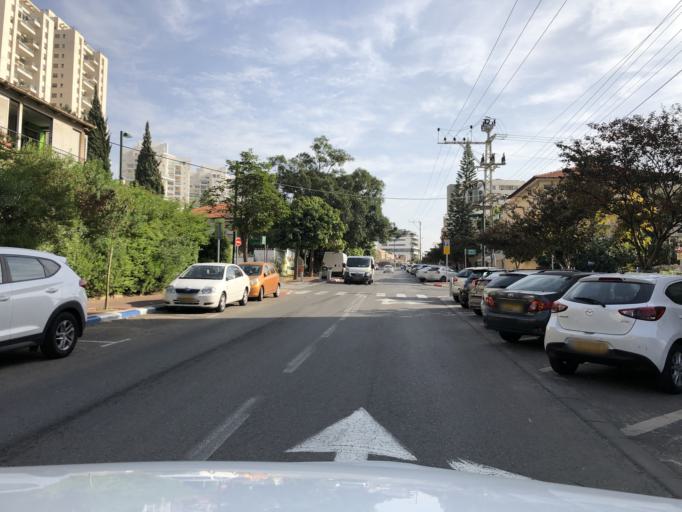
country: IL
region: Tel Aviv
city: Bene Beraq
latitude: 32.0700
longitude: 34.8304
